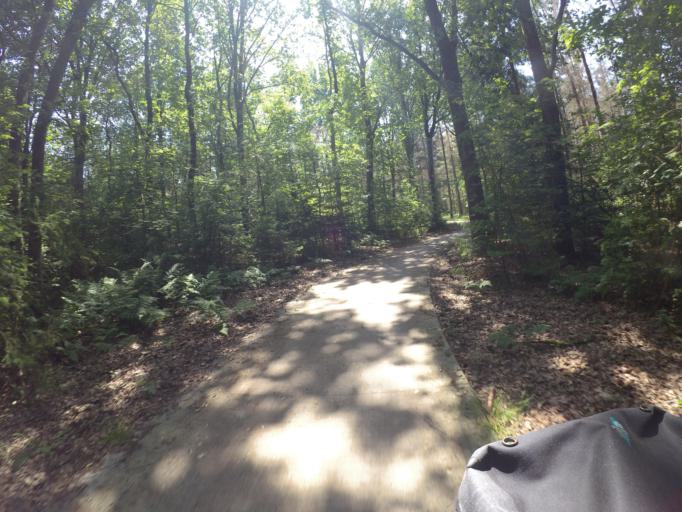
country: NL
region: Drenthe
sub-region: Gemeente De Wolden
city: Ruinen
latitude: 52.7270
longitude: 6.3581
